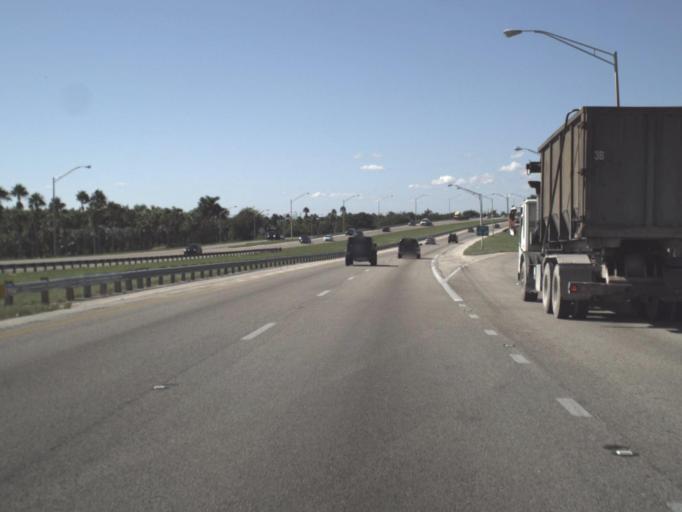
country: US
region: Florida
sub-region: Miami-Dade County
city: Goulds
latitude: 25.5360
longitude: -80.3672
